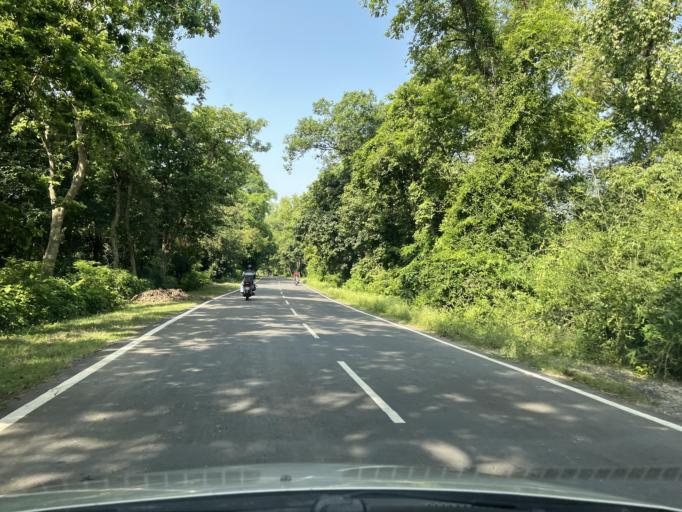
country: IN
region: Uttarakhand
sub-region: Naini Tal
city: Kaladhungi
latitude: 29.2250
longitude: 79.2442
